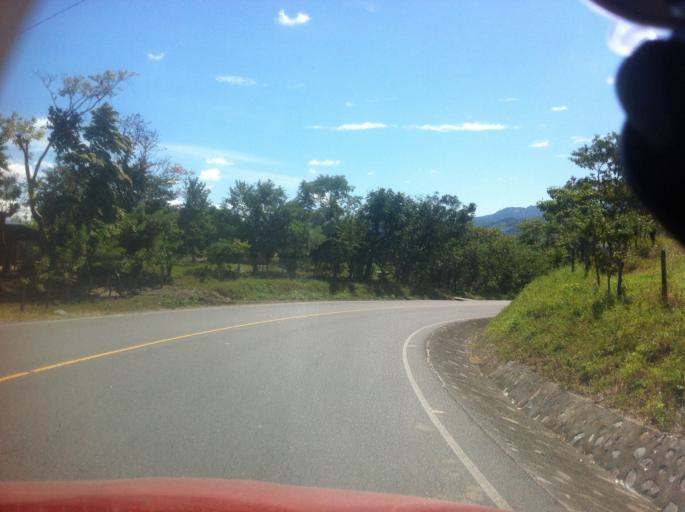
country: NI
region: Matagalpa
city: San Ramon
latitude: 12.8815
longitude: -85.8341
